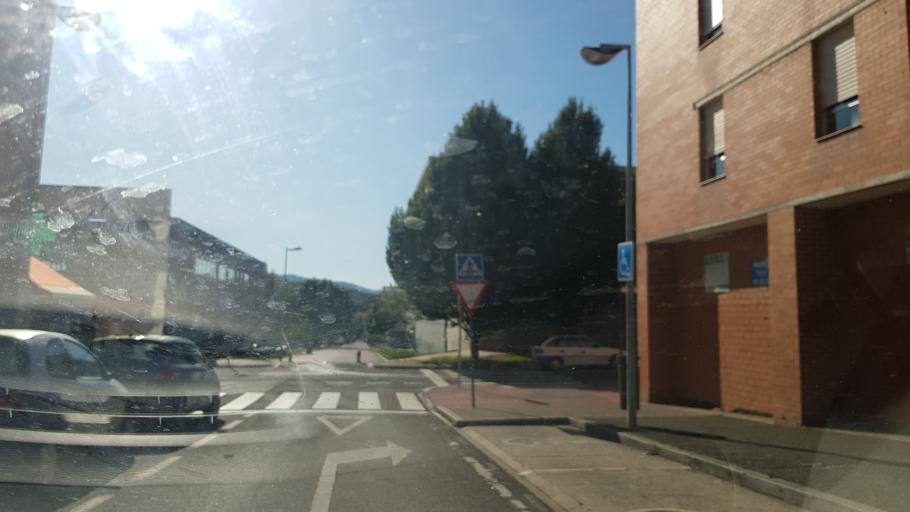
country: ES
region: Navarre
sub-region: Provincia de Navarra
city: Burlata
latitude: 42.8090
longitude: -1.6188
